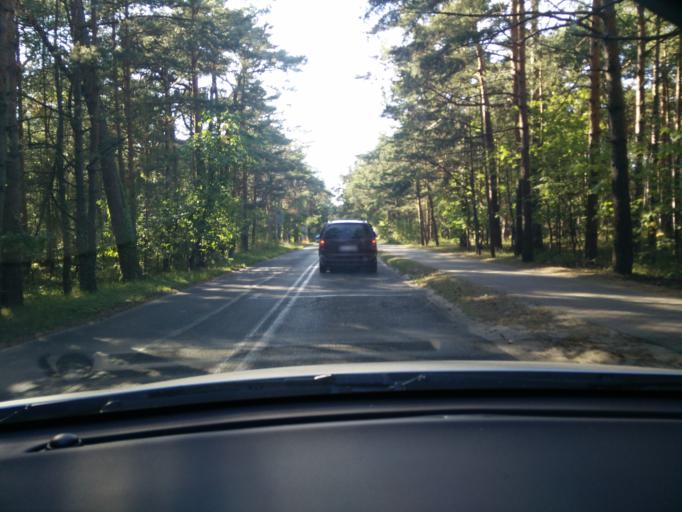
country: PL
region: Pomeranian Voivodeship
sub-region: Powiat pucki
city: Jastarnia
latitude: 54.6778
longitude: 18.7236
